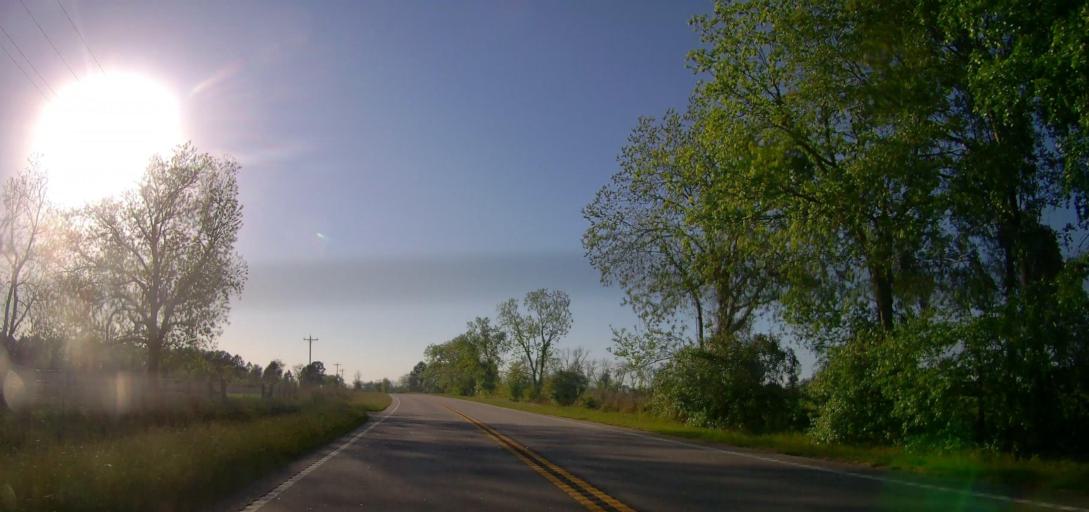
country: US
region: Georgia
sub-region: Ben Hill County
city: Fitzgerald
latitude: 31.7134
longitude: -83.1714
